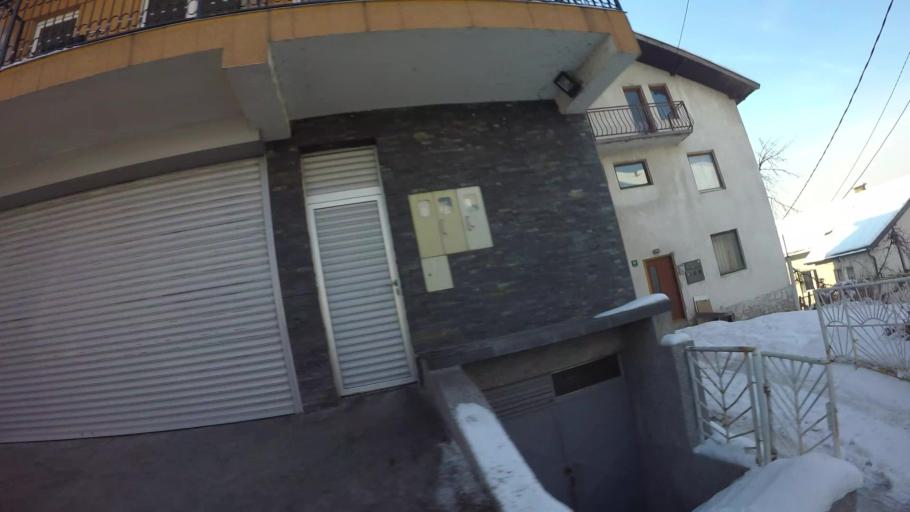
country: BA
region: Federation of Bosnia and Herzegovina
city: Kobilja Glava
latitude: 43.8498
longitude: 18.4059
